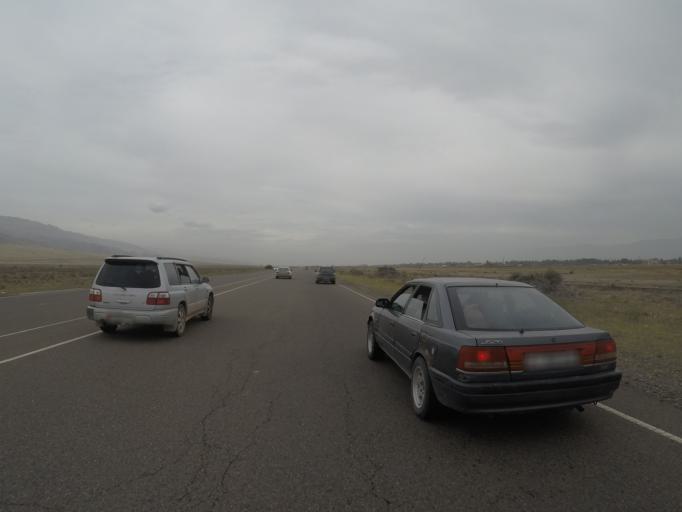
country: KG
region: Chuy
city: Bystrovka
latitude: 42.8301
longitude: 75.5055
